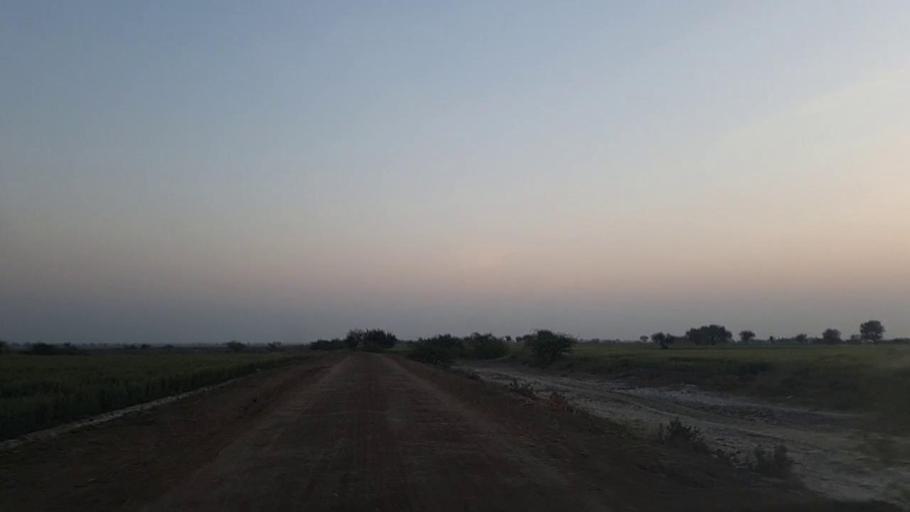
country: PK
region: Sindh
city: Naukot
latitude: 24.9960
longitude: 69.4335
